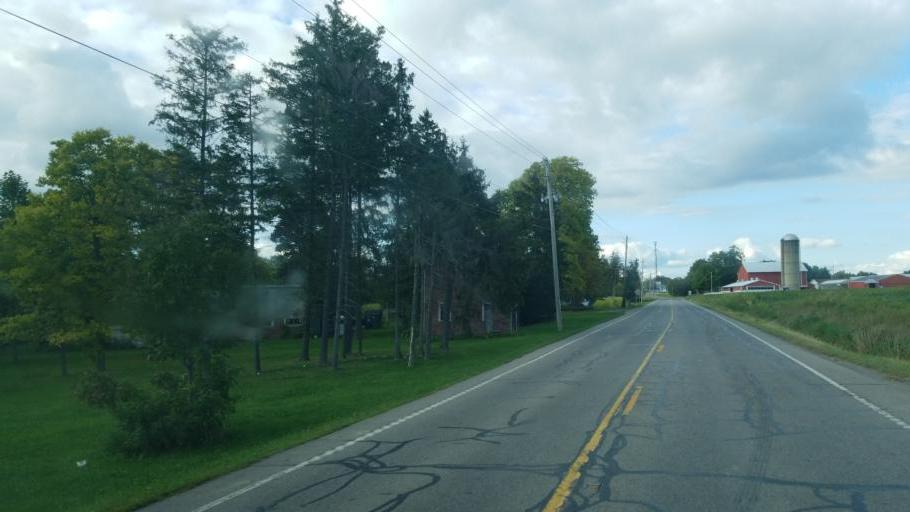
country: US
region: Ohio
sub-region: Huron County
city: Greenwich
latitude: 40.9021
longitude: -82.5007
